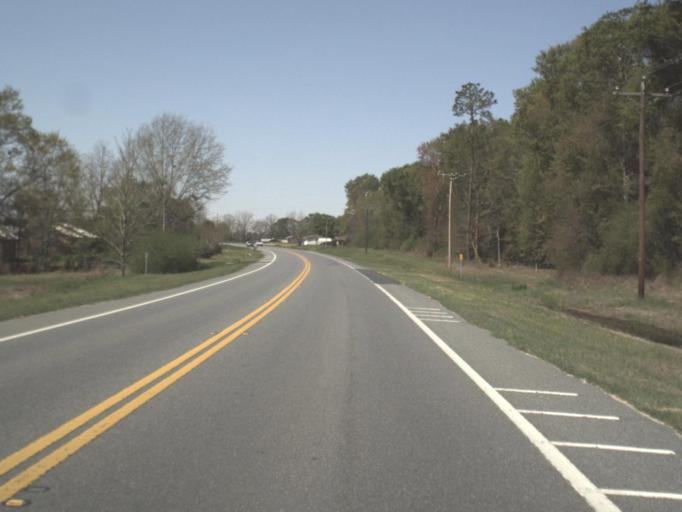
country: US
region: Florida
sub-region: Jackson County
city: Graceville
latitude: 30.9644
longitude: -85.5707
